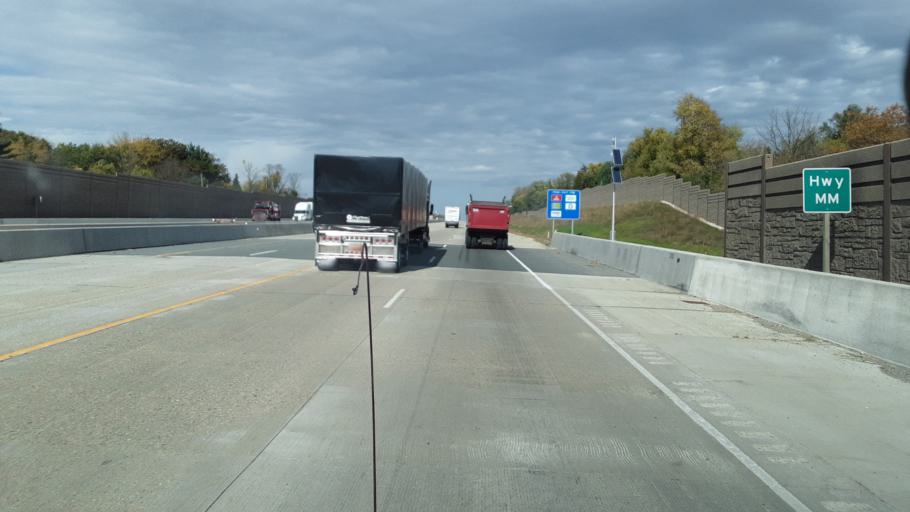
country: US
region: Wisconsin
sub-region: Rock County
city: Janesville
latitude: 42.6843
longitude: -88.9838
